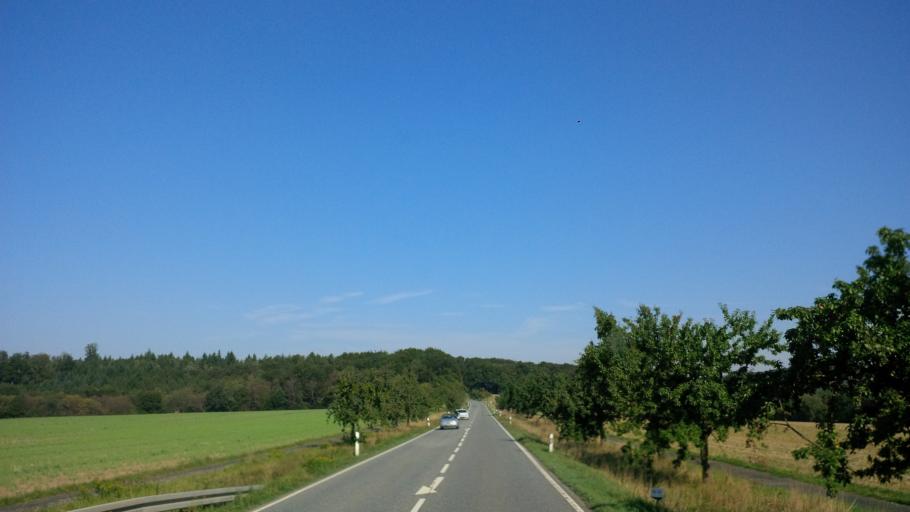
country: DE
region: Hesse
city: Weilmunster
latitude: 50.4548
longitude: 8.3897
